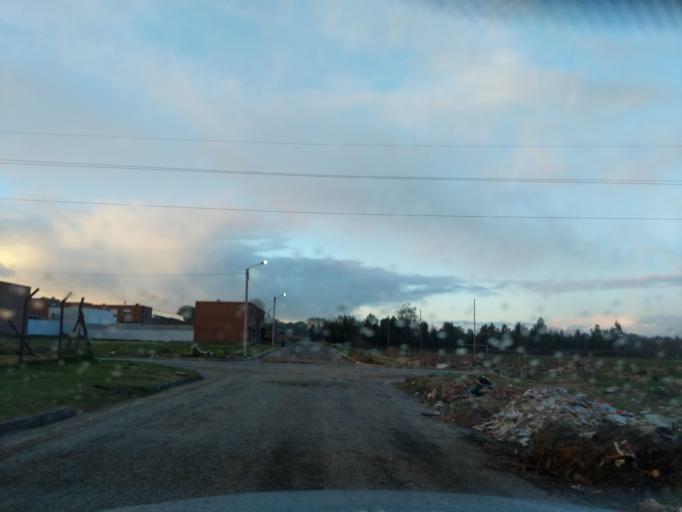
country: UY
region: Florida
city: Florida
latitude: -34.1049
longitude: -56.2063
